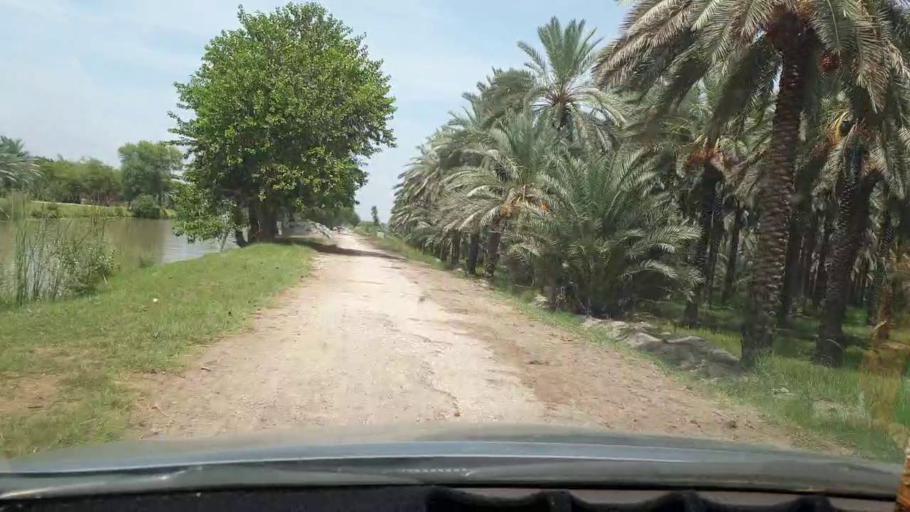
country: PK
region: Sindh
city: Khairpur
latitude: 27.4532
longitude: 68.7990
